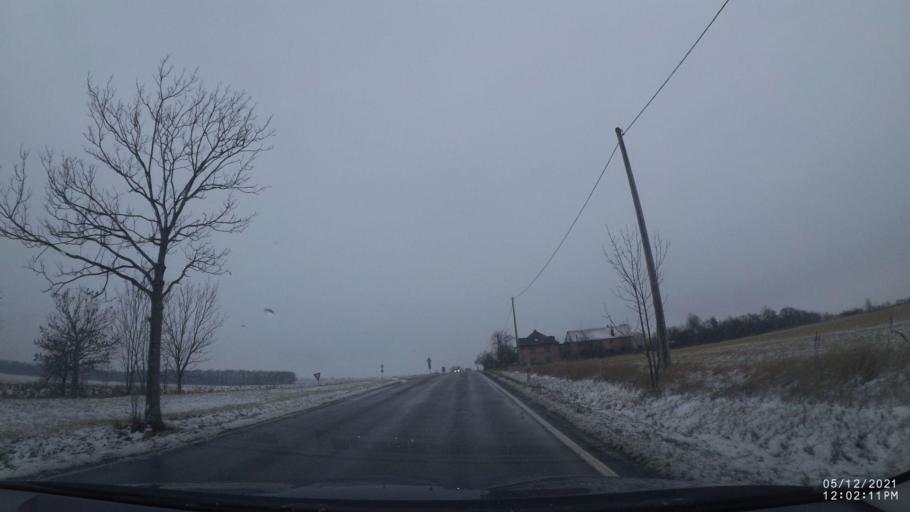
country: CZ
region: Kralovehradecky
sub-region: Okres Rychnov nad Kneznou
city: Opocno
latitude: 50.2779
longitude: 16.0836
